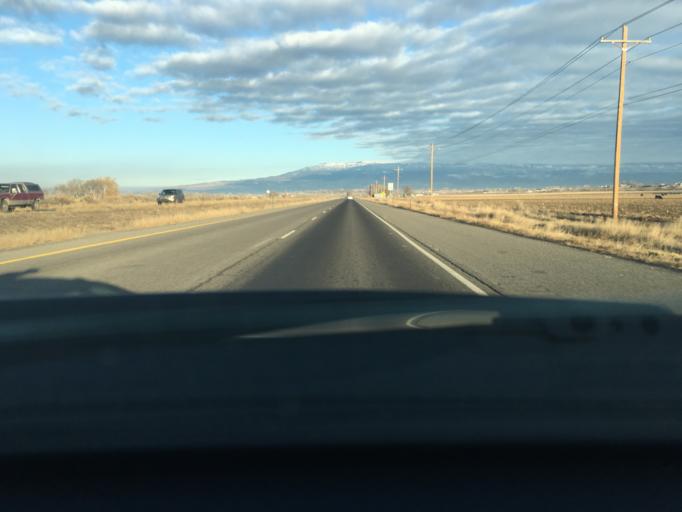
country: US
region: Colorado
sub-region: Montrose County
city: Olathe
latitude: 38.6801
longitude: -108.0071
